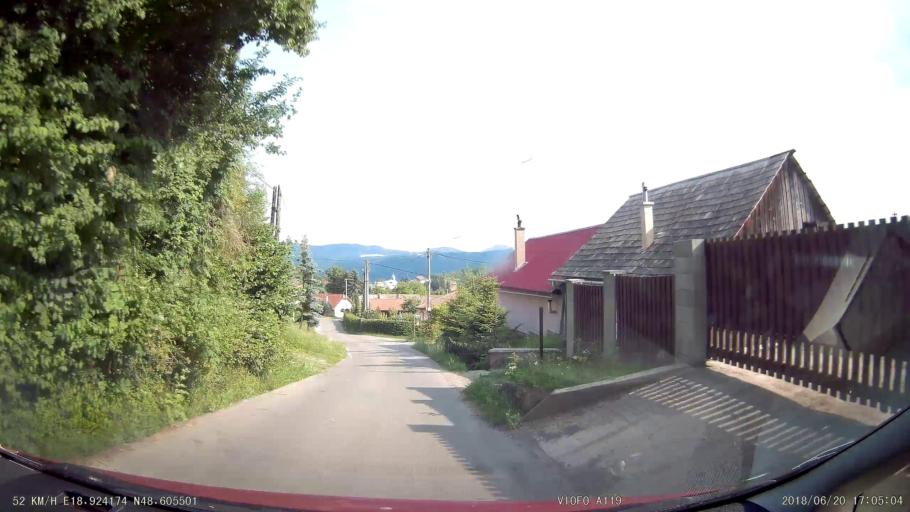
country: SK
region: Banskobystricky
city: Ziar nad Hronom
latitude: 48.6052
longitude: 18.9242
